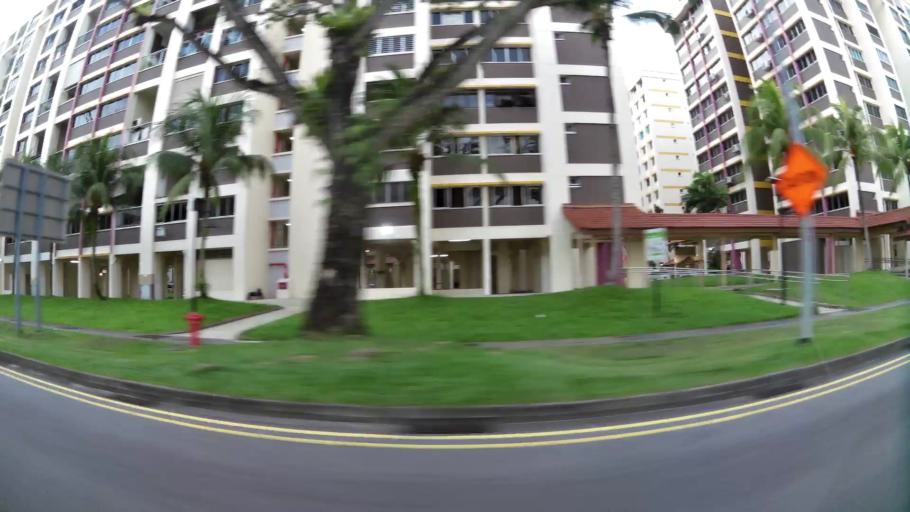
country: MY
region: Johor
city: Kampung Pasir Gudang Baru
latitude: 1.4290
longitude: 103.8494
